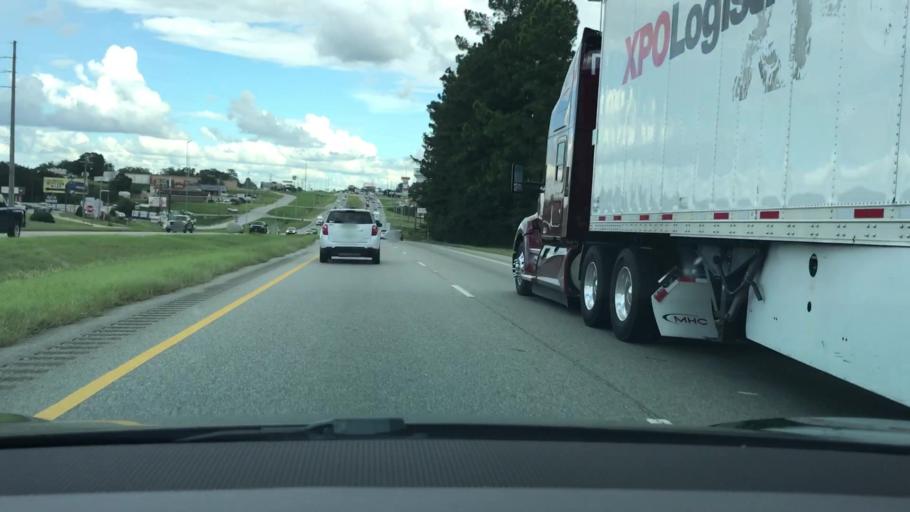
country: US
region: Alabama
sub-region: Pike County
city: Troy
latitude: 31.7889
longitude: -85.9717
